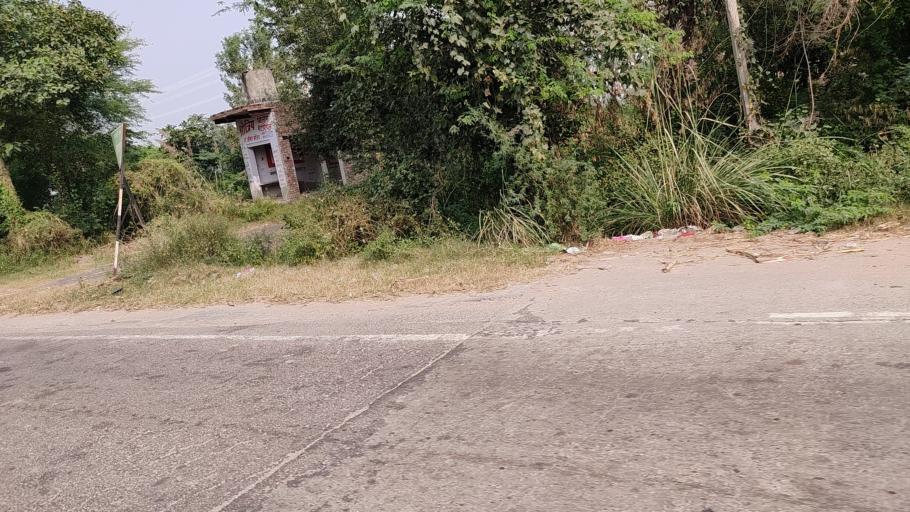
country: IN
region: Uttar Pradesh
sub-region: Mathura
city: Barsana
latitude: 27.6590
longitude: 77.3823
